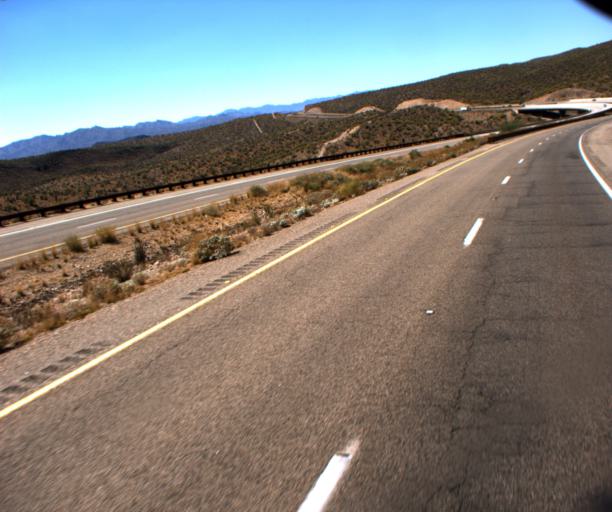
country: US
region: Arizona
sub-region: Yavapai County
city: Bagdad
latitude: 34.5745
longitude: -113.4890
